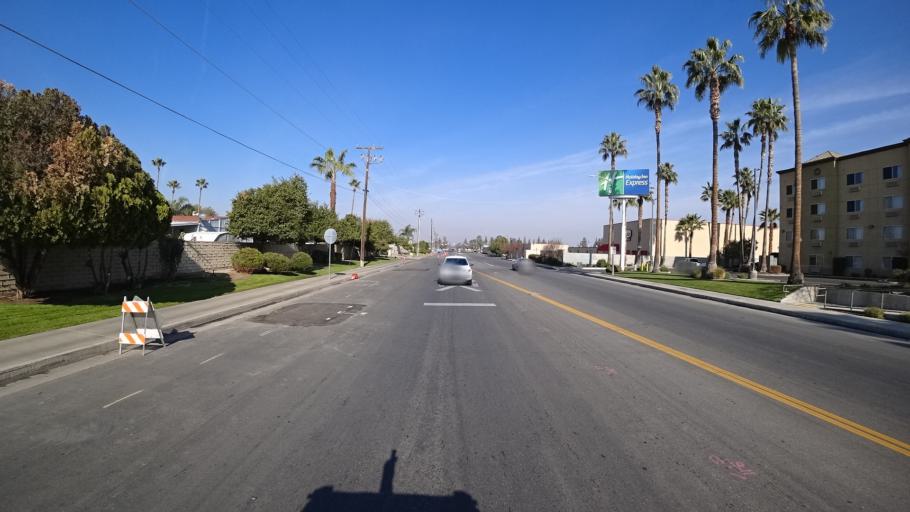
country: US
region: California
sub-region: Kern County
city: Greenfield
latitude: 35.3151
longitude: -119.0301
